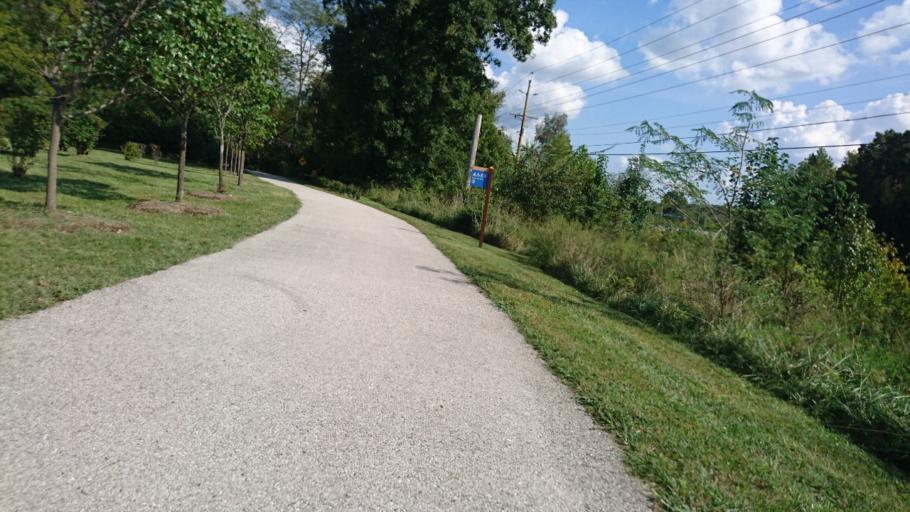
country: US
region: Missouri
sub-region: Saint Louis County
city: Eureka
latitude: 38.5484
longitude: -90.6317
